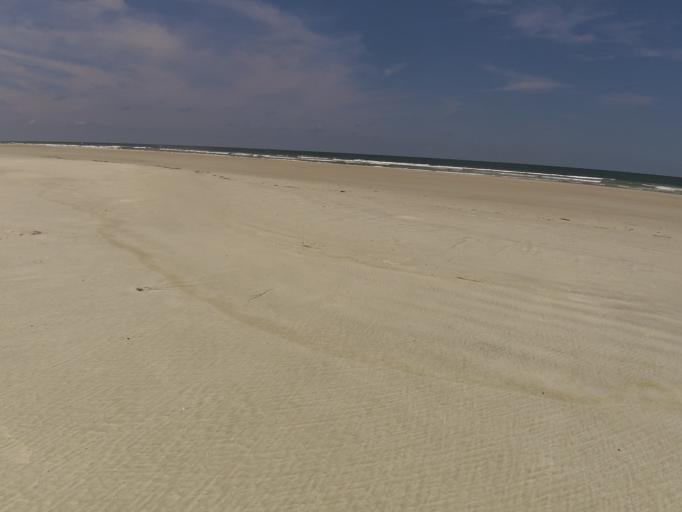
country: US
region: Florida
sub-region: Duval County
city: Atlantic Beach
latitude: 30.4391
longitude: -81.4081
